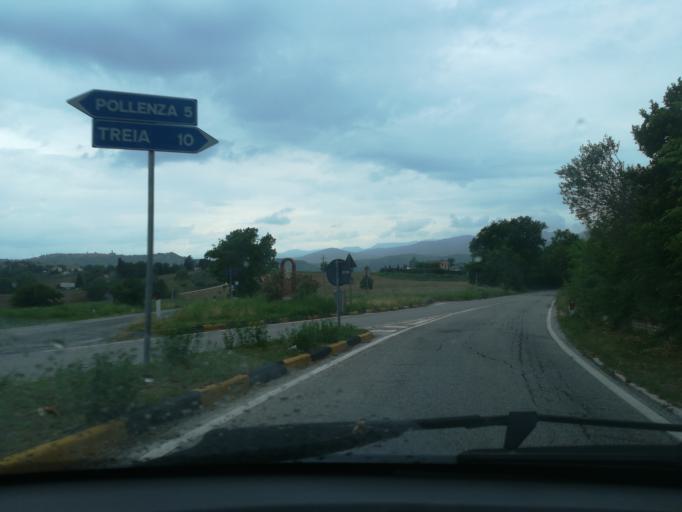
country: IT
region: The Marches
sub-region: Provincia di Macerata
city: Casette Verdini
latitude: 43.2857
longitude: 13.3945
